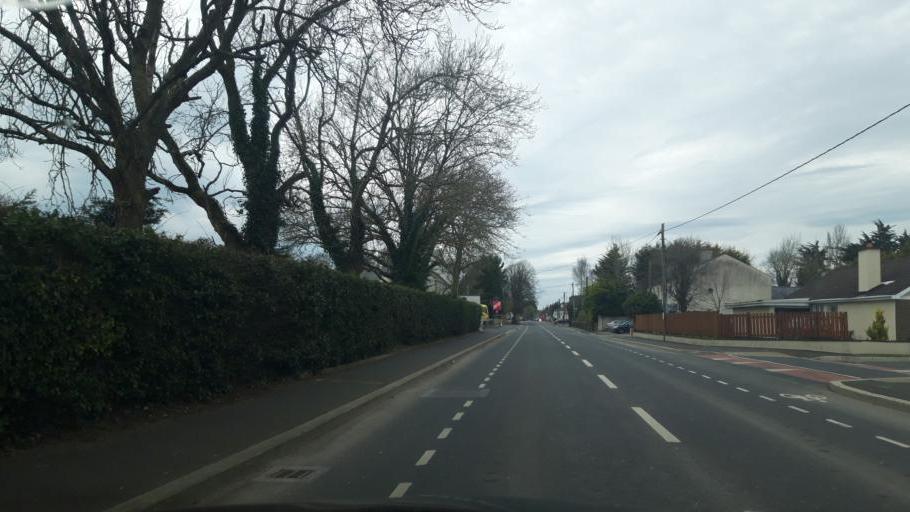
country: IE
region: Leinster
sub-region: Kildare
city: Prosperous
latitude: 53.2890
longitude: -6.7525
